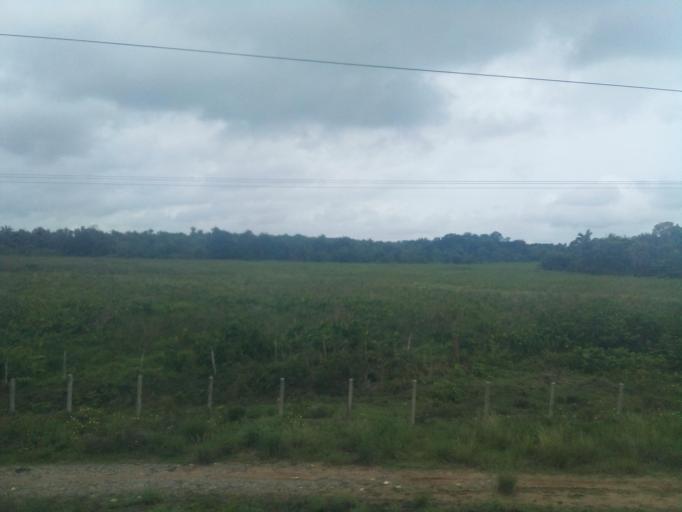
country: BR
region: Maranhao
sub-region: Vitoria Do Mearim
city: Vitoria do Mearim
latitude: -3.5534
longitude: -44.8218
